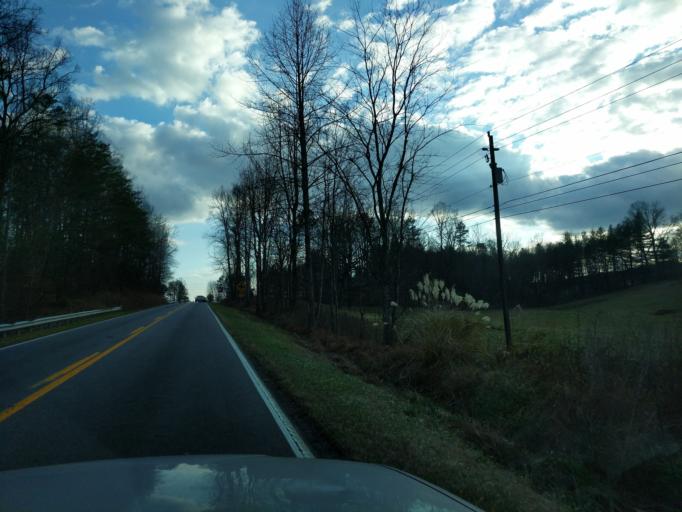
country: US
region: North Carolina
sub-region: McDowell County
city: West Marion
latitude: 35.6193
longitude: -81.9860
